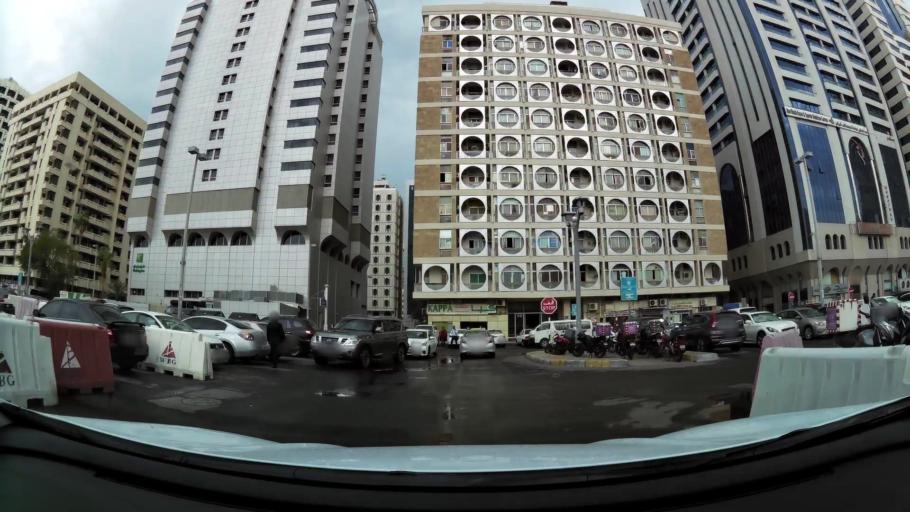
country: AE
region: Abu Dhabi
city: Abu Dhabi
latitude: 24.4887
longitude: 54.3688
